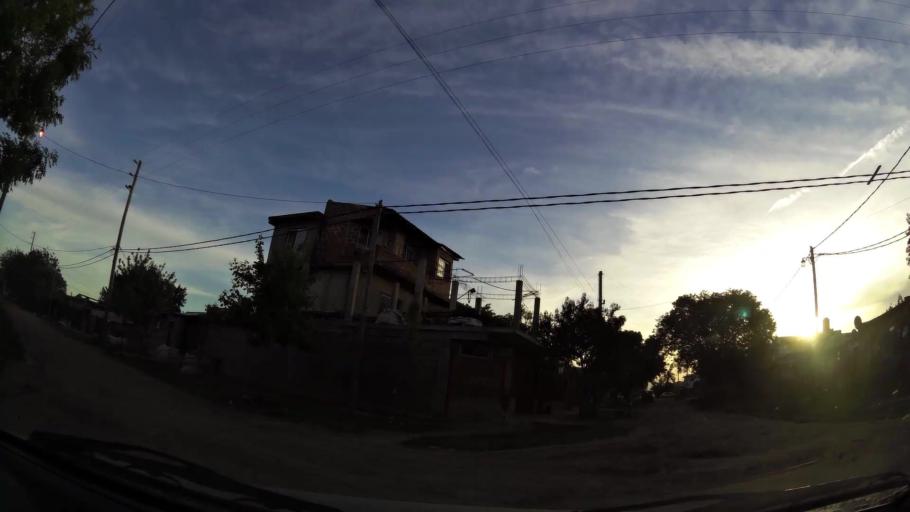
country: AR
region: Buenos Aires
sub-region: Partido de Almirante Brown
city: Adrogue
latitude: -34.7800
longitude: -58.3414
